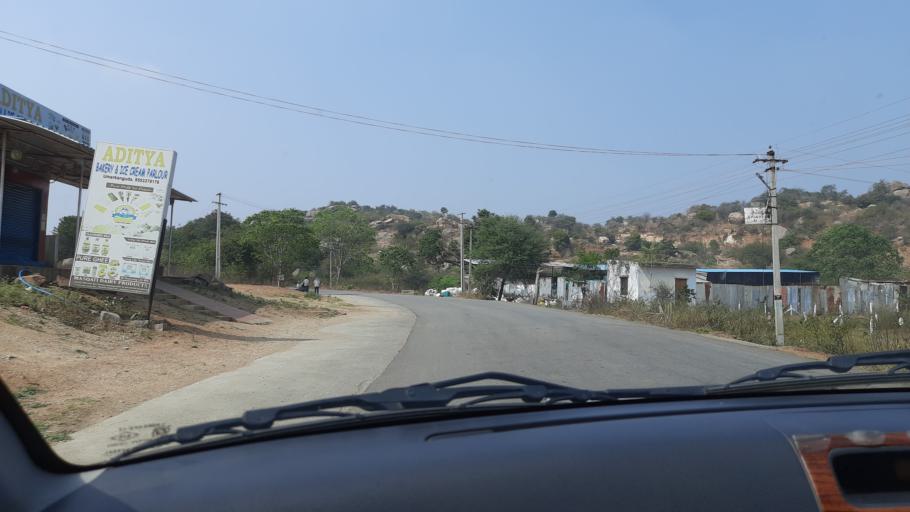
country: IN
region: Telangana
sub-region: Rangareddi
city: Lal Bahadur Nagar
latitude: 17.2747
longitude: 78.6671
